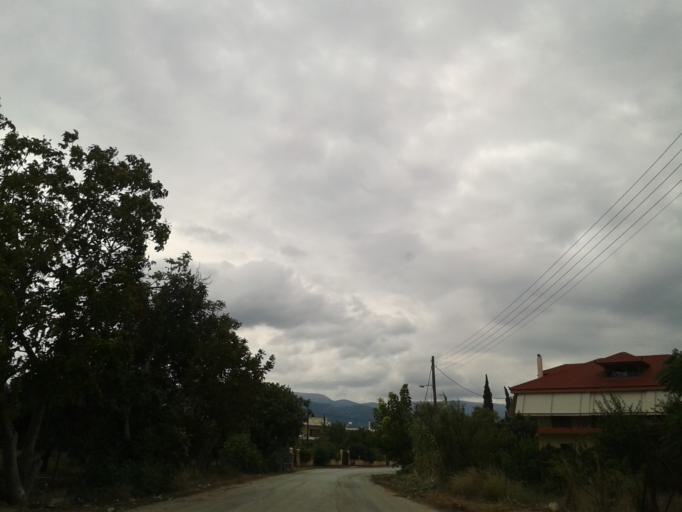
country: GR
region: Peloponnese
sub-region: Nomos Argolidos
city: Nea Kios
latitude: 37.5951
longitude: 22.6938
